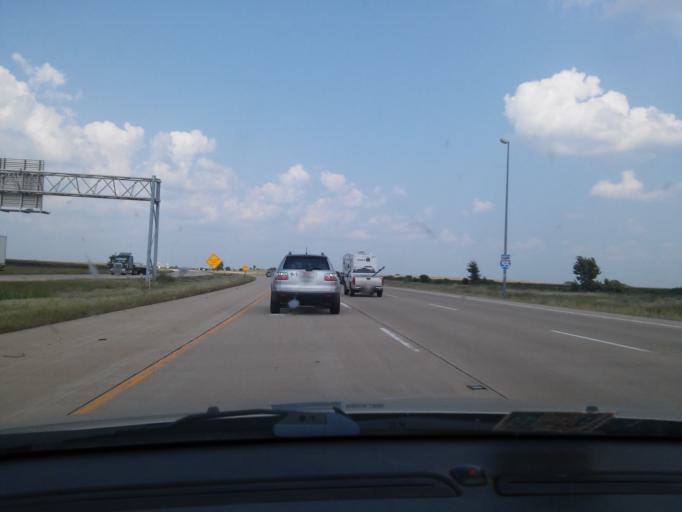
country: US
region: Illinois
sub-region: McLean County
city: Normal
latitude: 40.5398
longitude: -88.9380
